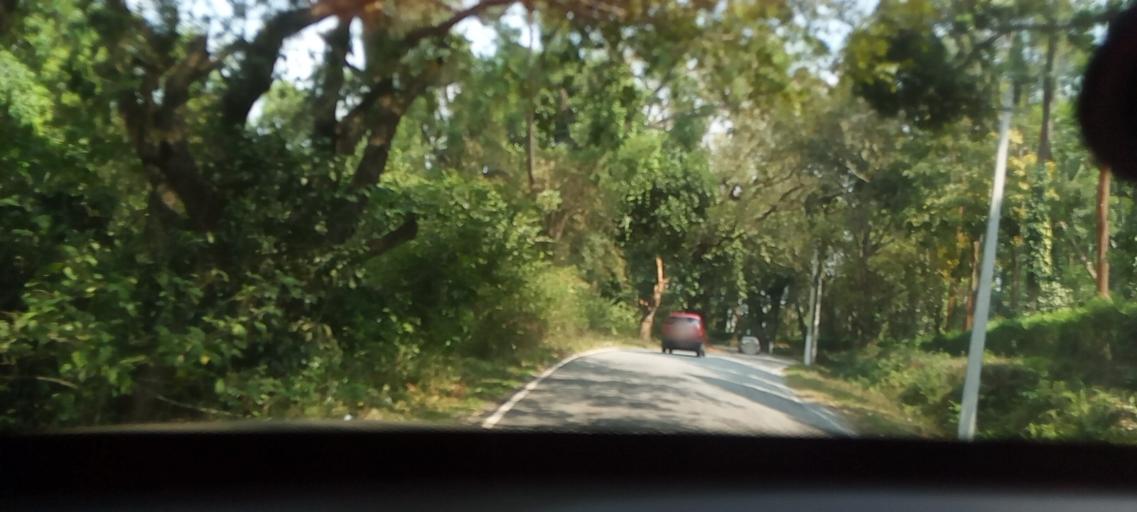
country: IN
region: Karnataka
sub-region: Chikmagalur
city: Chikmagalur
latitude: 13.2561
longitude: 75.6667
